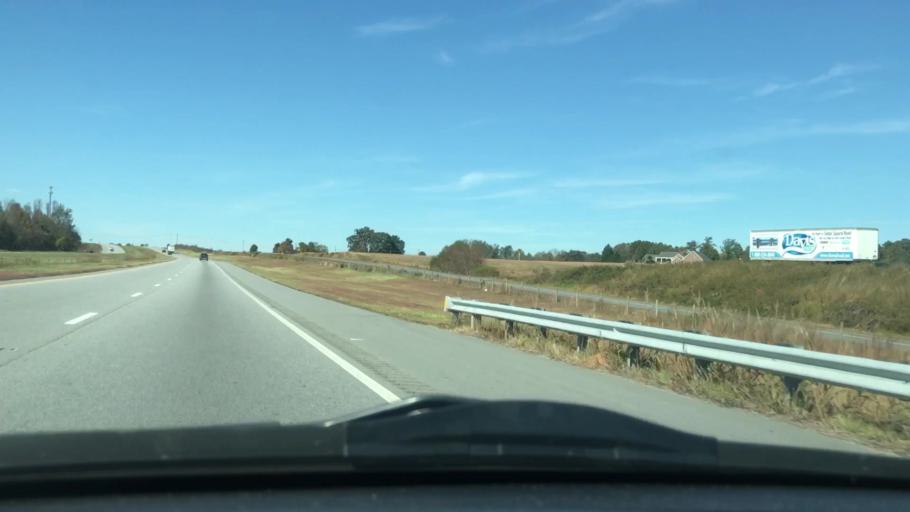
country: US
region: North Carolina
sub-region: Randolph County
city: Archdale
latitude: 35.8639
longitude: -79.8900
